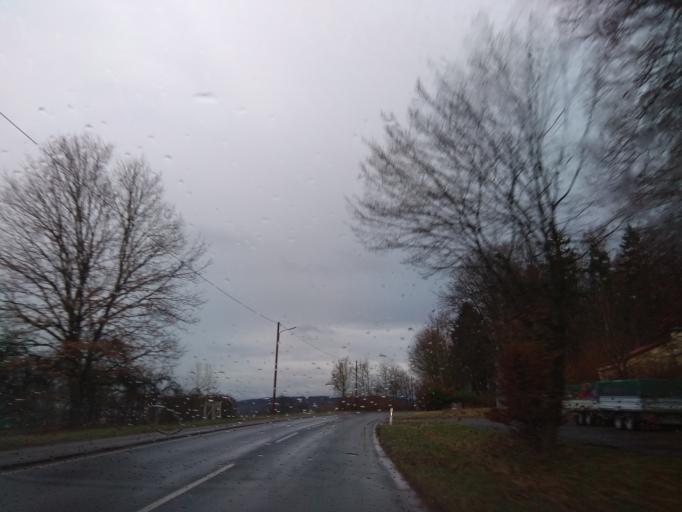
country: DE
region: Baden-Wuerttemberg
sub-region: Regierungsbezirk Stuttgart
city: Steinenbronn
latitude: 48.7016
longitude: 9.1166
